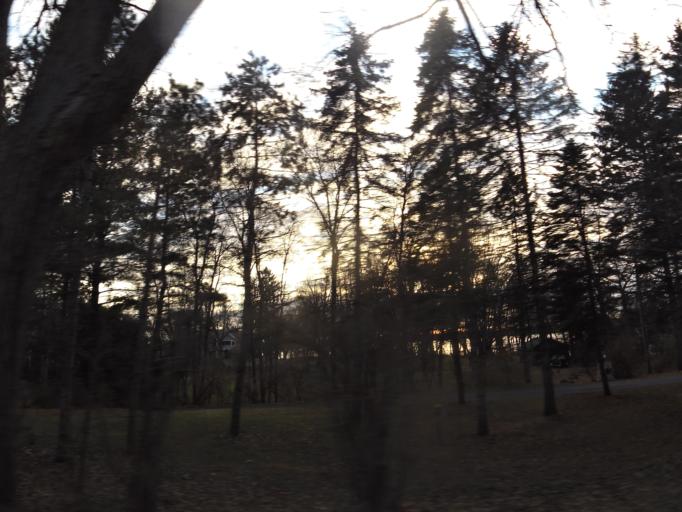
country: US
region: Minnesota
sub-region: Washington County
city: Dellwood
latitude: 45.0956
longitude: -92.9826
